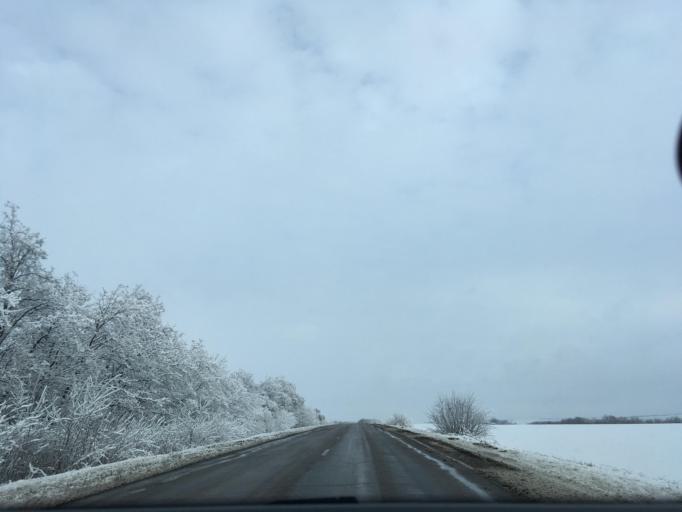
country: UA
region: Luhansk
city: Lozno-Oleksandrivka
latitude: 49.9914
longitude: 39.0227
